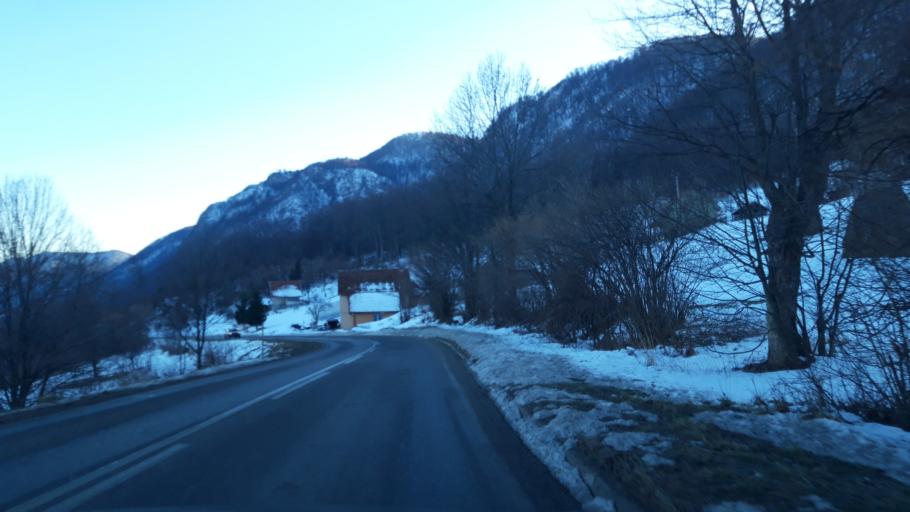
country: BA
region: Republika Srpska
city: Vlasenica
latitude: 44.1595
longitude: 18.9468
